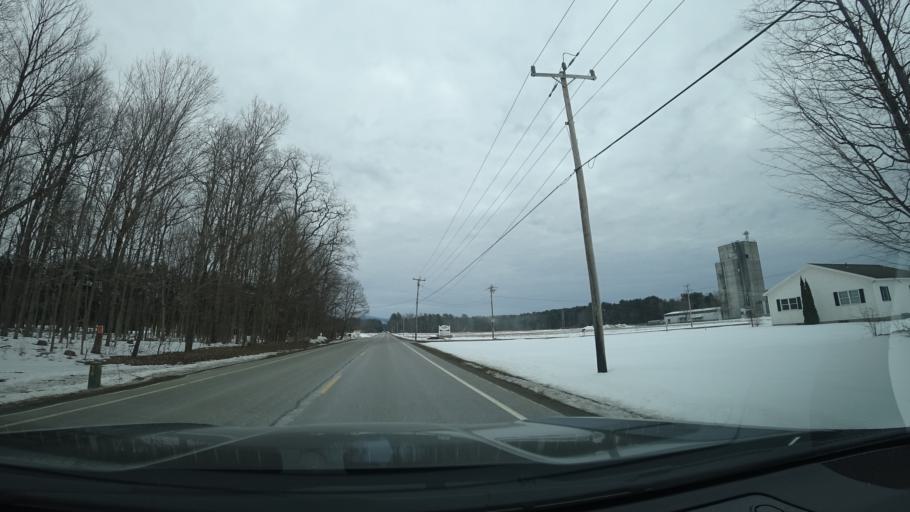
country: US
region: New York
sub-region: Washington County
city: Cambridge
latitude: 43.1500
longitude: -73.3811
